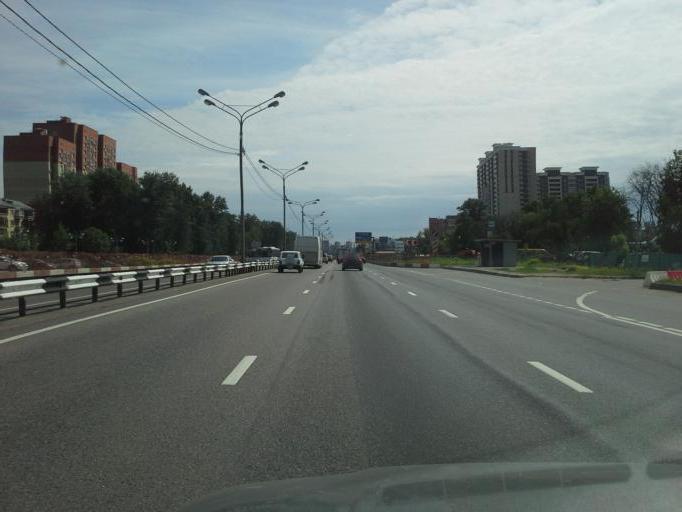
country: RU
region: Moskovskaya
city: Saltykovka
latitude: 55.7937
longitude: 37.9262
